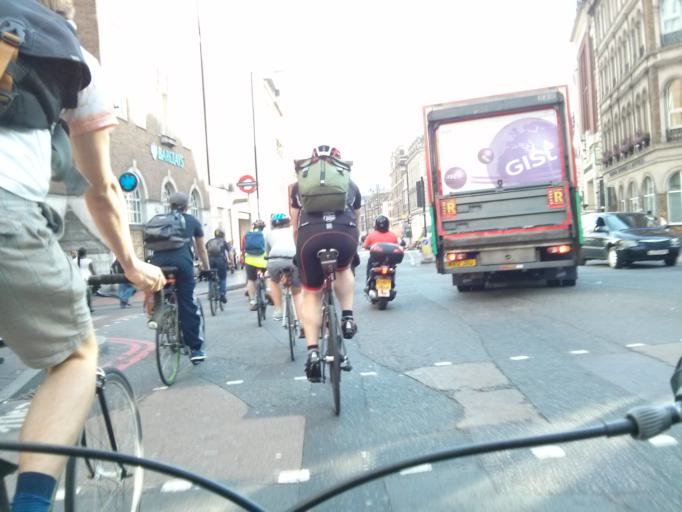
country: GB
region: England
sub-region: Greater London
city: City of London
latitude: 51.5053
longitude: -0.0891
